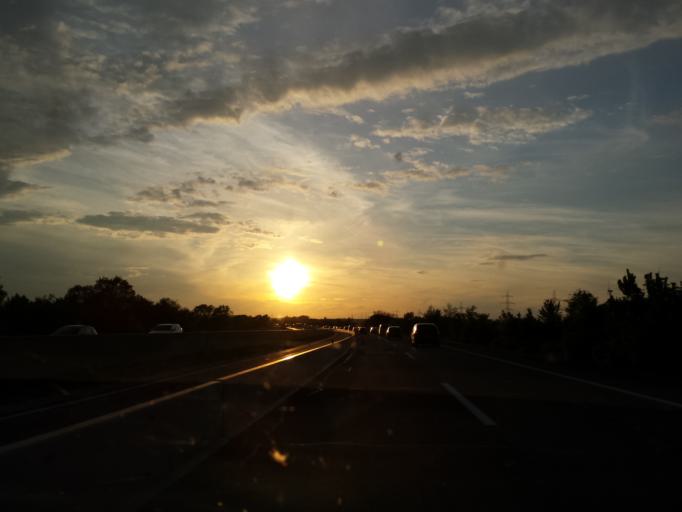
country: AT
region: Burgenland
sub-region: Politischer Bezirk Neusiedl am See
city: Parndorf
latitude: 47.9688
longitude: 16.8819
